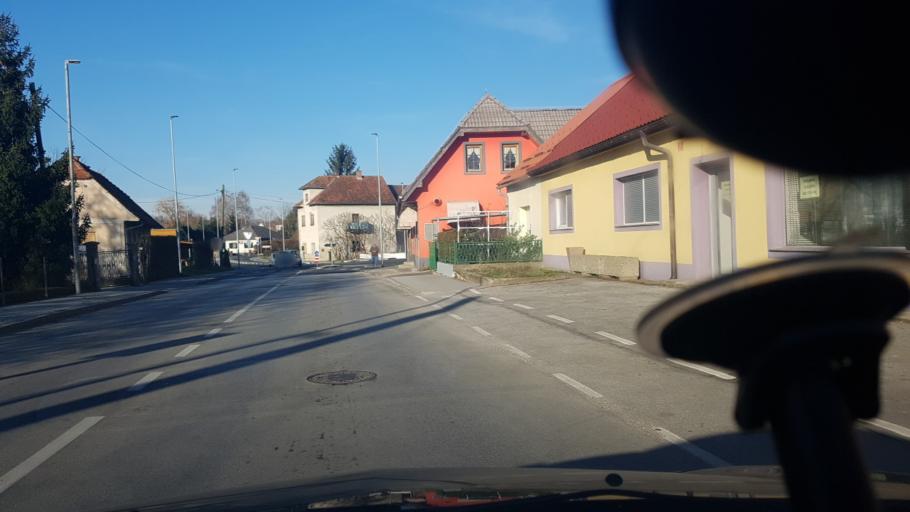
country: SI
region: Ptuj
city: Ptuj
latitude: 46.4143
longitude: 15.8645
